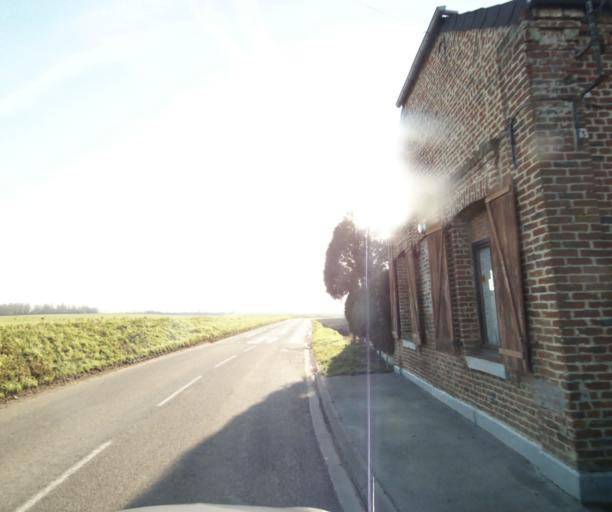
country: FR
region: Nord-Pas-de-Calais
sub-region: Departement du Nord
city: Saultain
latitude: 50.3279
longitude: 3.5754
